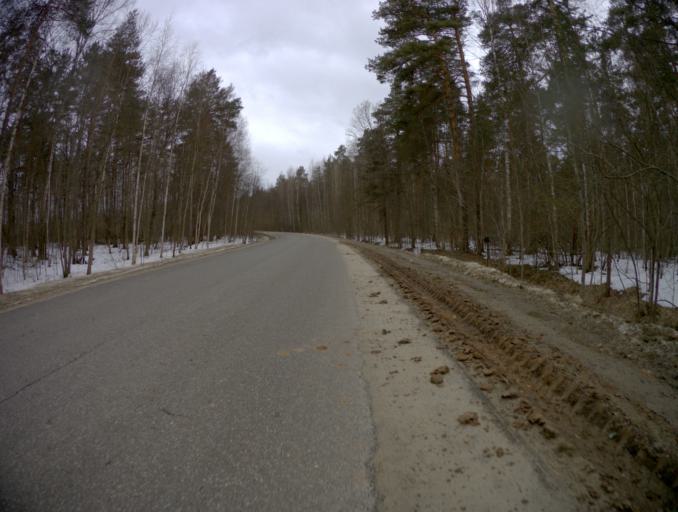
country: RU
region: Vladimir
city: Bogolyubovo
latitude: 56.1517
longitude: 40.5310
